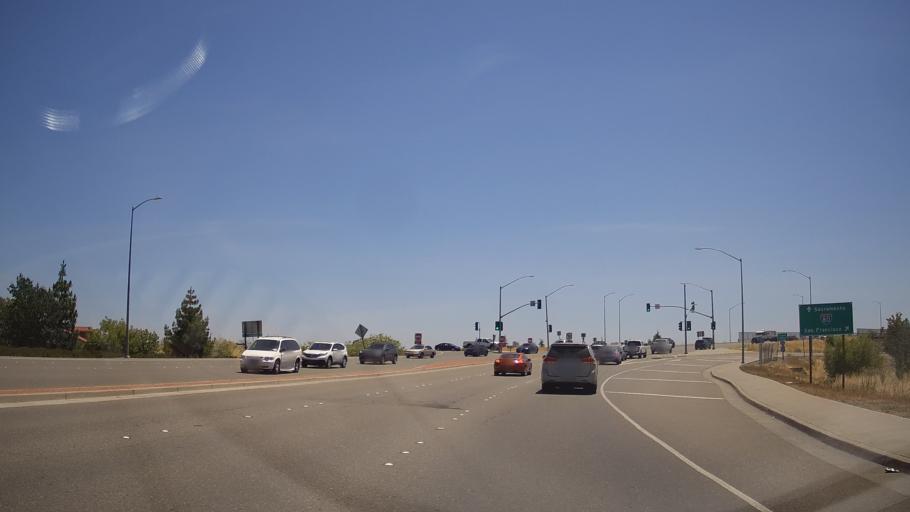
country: US
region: California
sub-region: Solano County
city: Hartley
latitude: 38.3900
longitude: -121.9359
